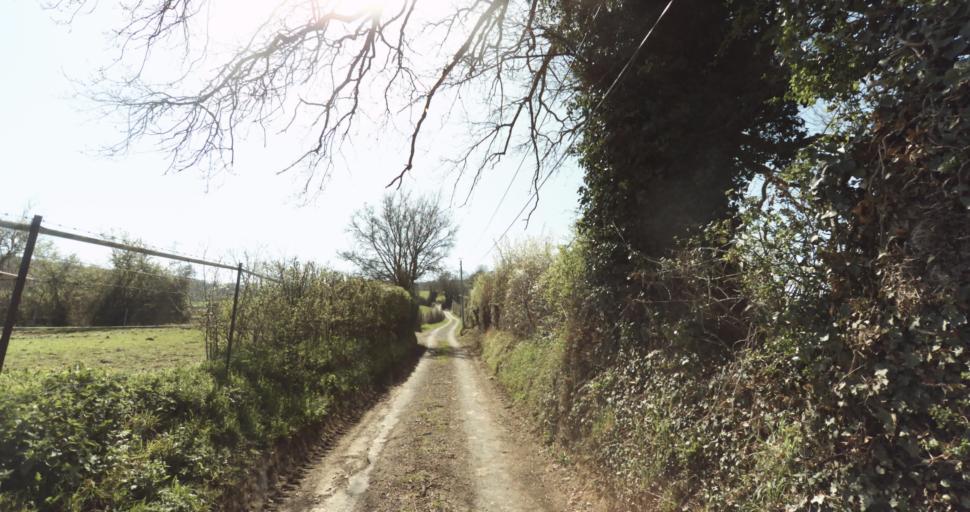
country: FR
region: Lower Normandy
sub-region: Departement du Calvados
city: Saint-Pierre-sur-Dives
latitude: 49.0162
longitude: 0.0443
